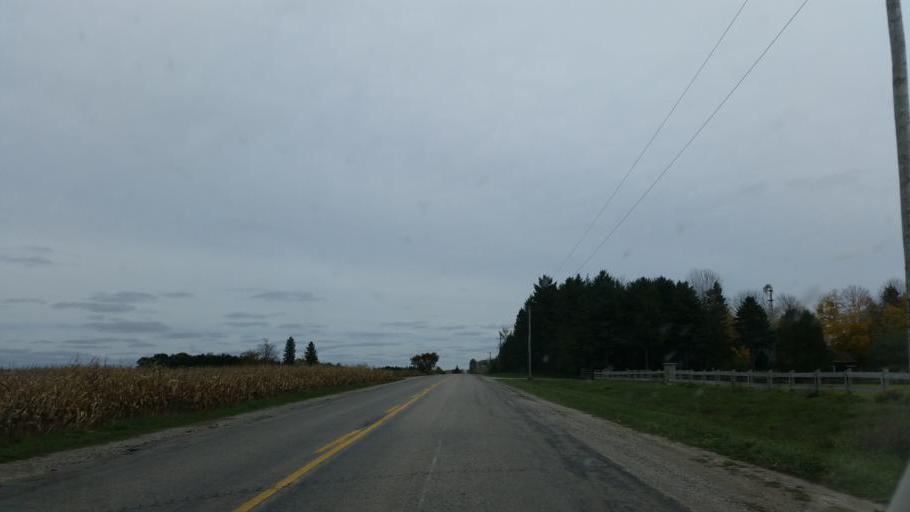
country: CA
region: Ontario
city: Wingham
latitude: 43.9961
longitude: -81.3184
